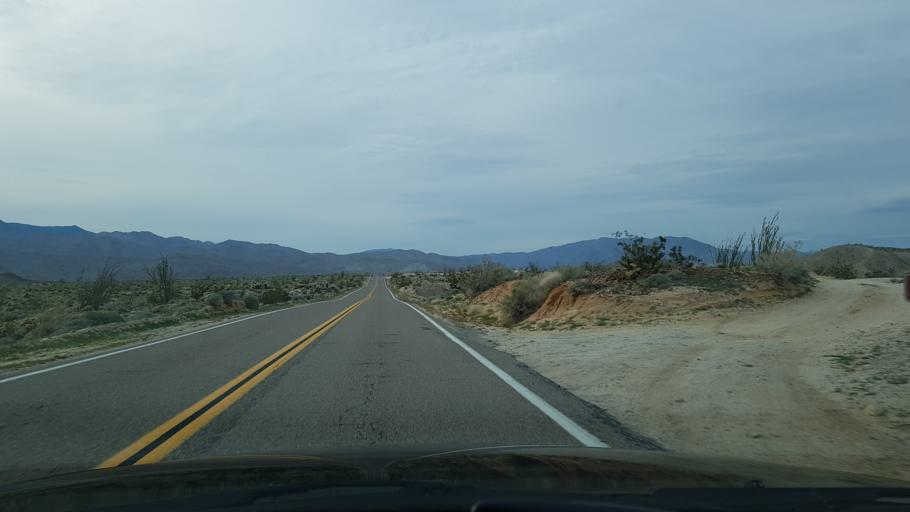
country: MX
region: Baja California
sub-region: Tecate
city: Cereso del Hongo
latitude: 32.8248
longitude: -116.1629
